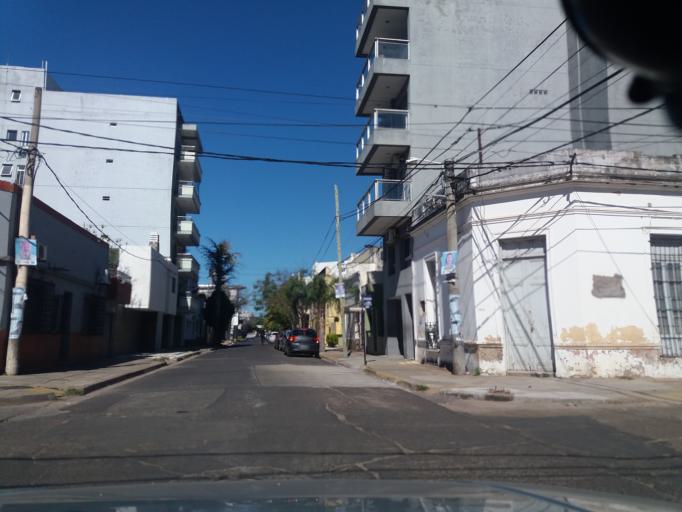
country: AR
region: Corrientes
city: Corrientes
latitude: -27.4716
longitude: -58.8420
